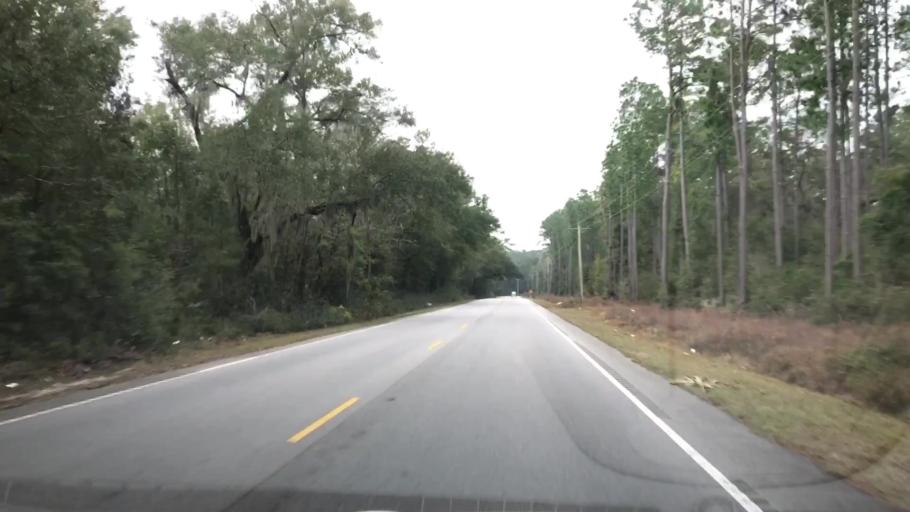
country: US
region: South Carolina
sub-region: Jasper County
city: Ridgeland
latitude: 32.4932
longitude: -80.8861
